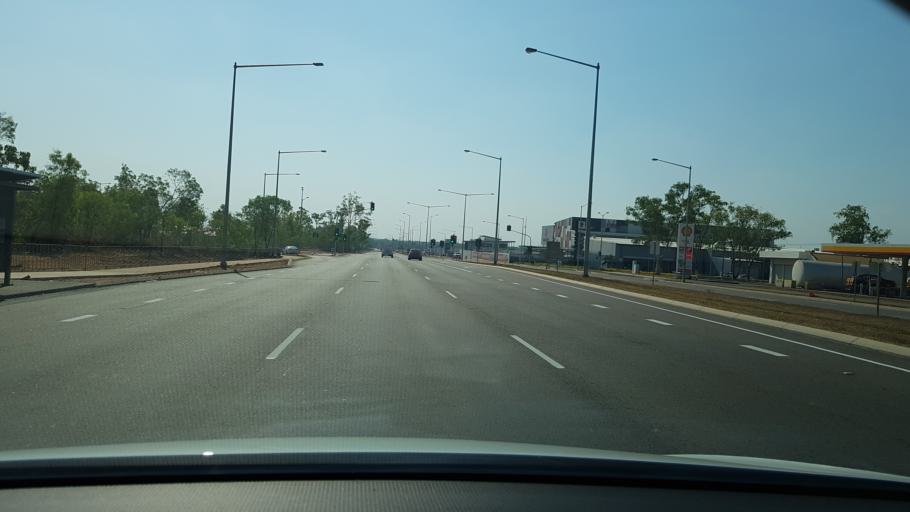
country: AU
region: Northern Territory
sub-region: Palmerston
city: Palmerston
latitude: -12.4743
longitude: 130.9839
